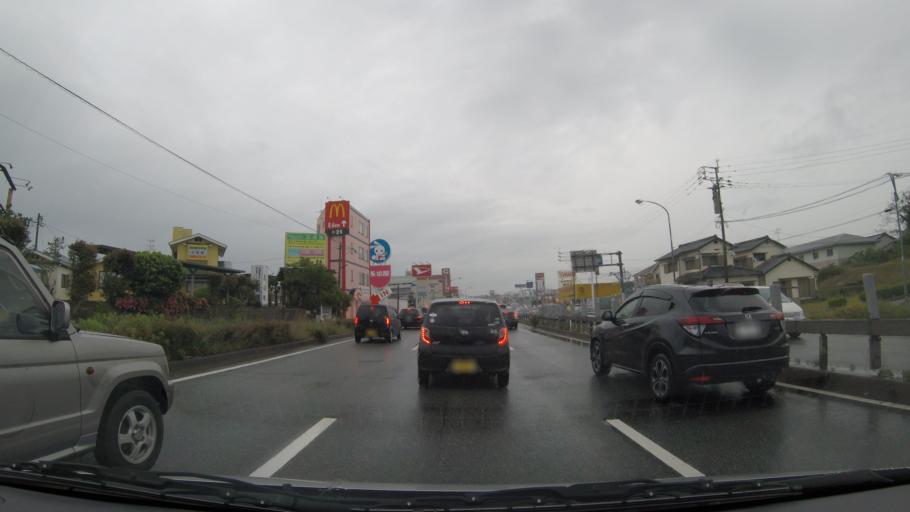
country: JP
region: Fukuoka
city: Shingu
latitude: 33.6978
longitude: 130.4512
